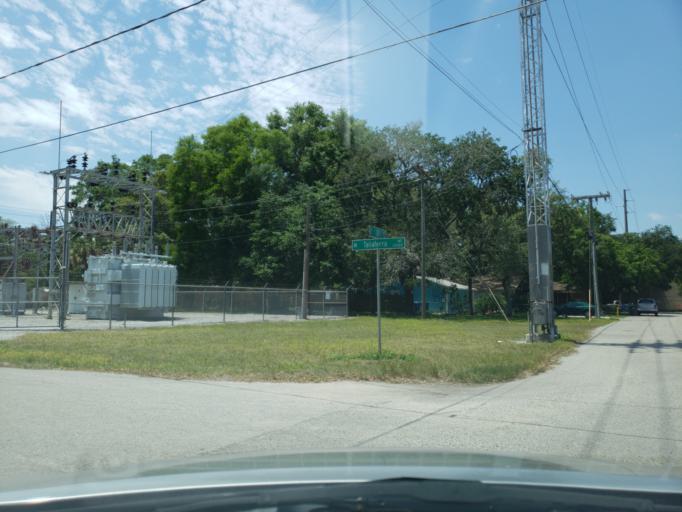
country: US
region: Florida
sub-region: Hillsborough County
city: University
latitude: 28.0656
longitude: -82.4532
